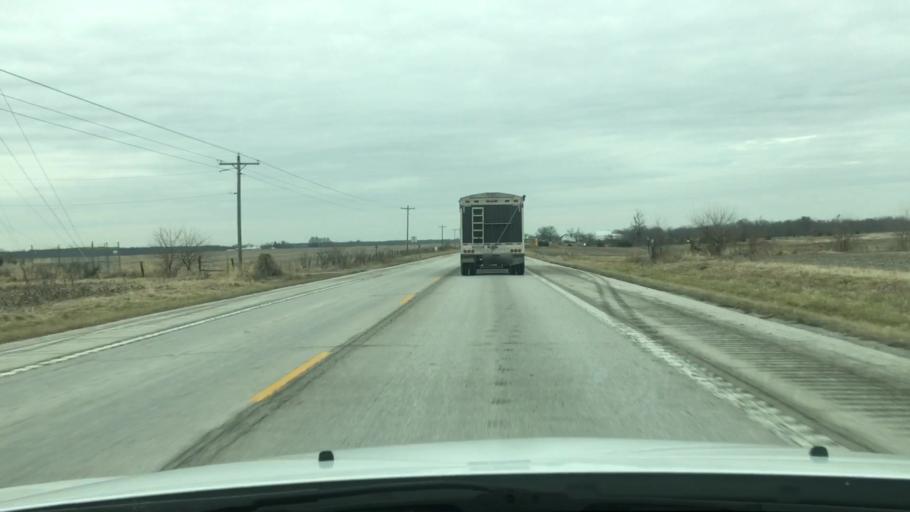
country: US
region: Missouri
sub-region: Montgomery County
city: Wellsville
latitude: 39.1698
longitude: -91.6477
